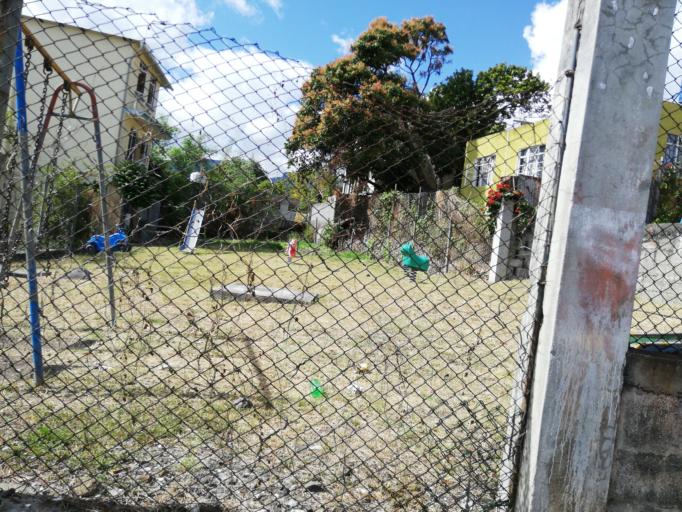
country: MU
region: Port Louis
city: Port Louis
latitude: -20.1675
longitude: 57.4941
